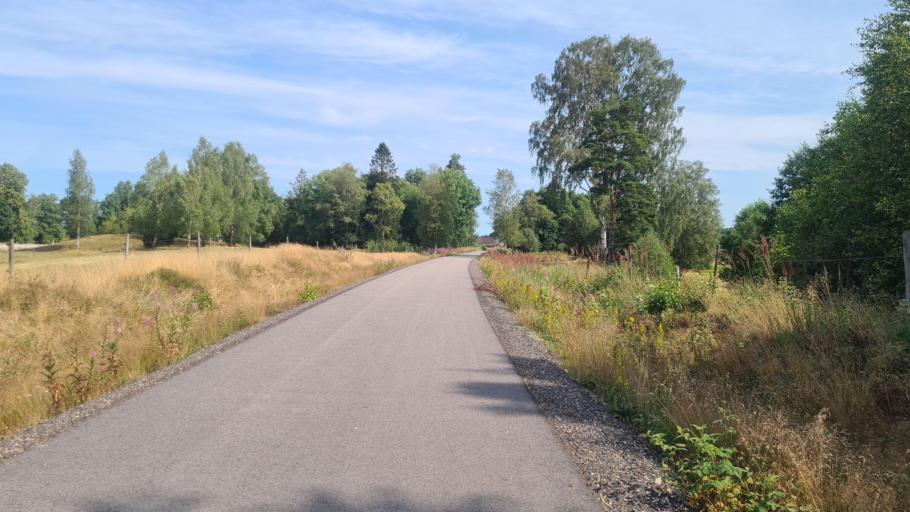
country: SE
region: Kronoberg
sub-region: Ljungby Kommun
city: Lagan
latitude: 56.8707
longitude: 13.9797
